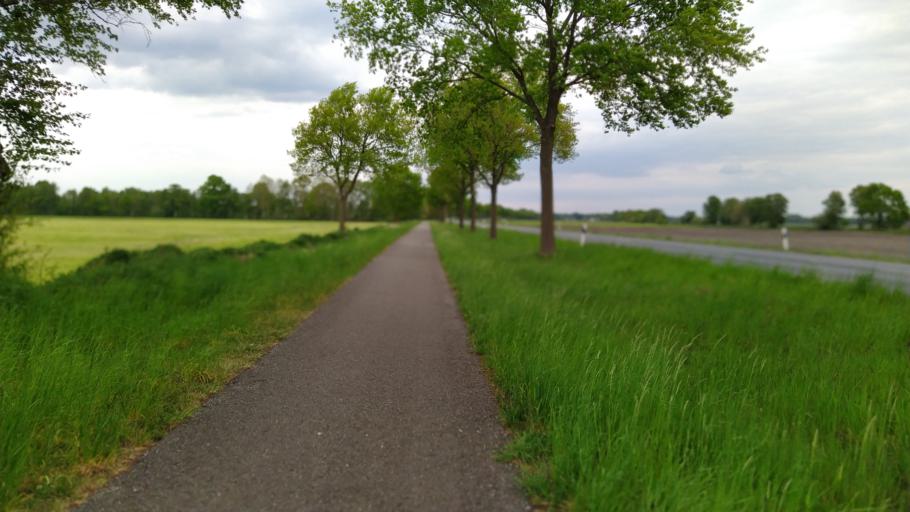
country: DE
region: Lower Saxony
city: Tarmstedt
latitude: 53.2078
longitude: 9.0389
